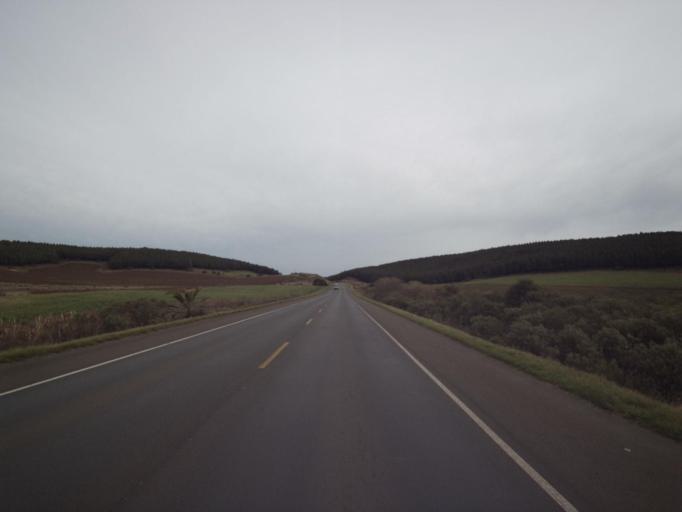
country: BR
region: Parana
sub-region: Palmas
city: Palmas
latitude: -26.6626
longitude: -51.5434
